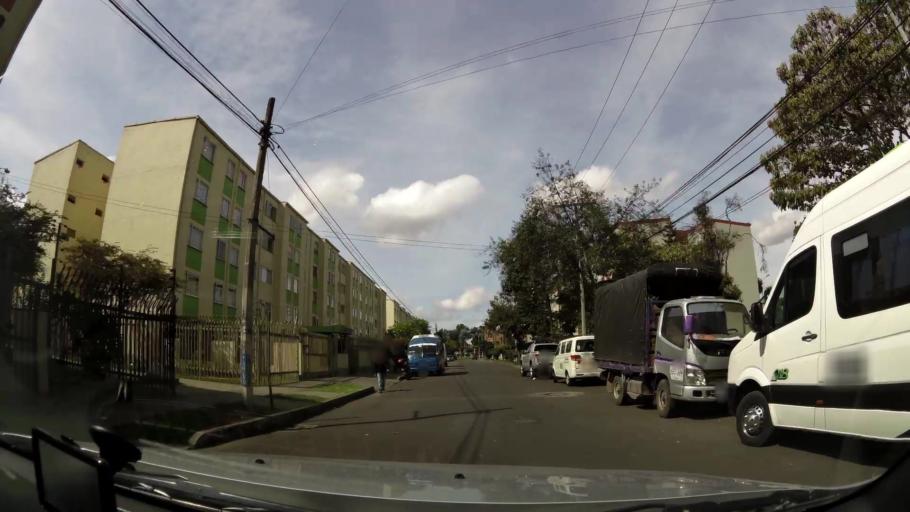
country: CO
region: Bogota D.C.
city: Bogota
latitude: 4.6436
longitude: -74.1339
